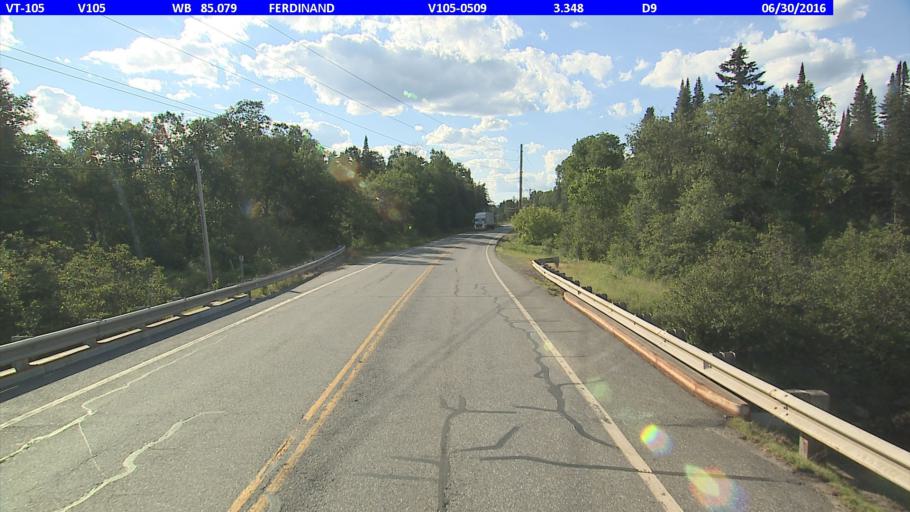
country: US
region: New Hampshire
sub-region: Coos County
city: Stratford
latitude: 44.7714
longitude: -71.7419
